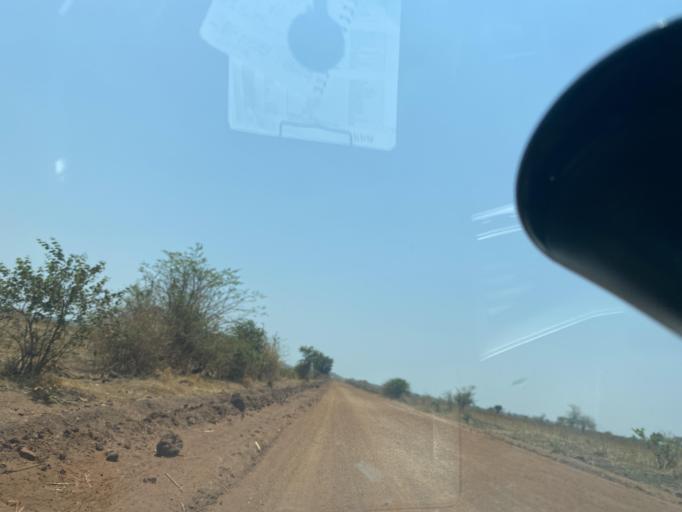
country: ZM
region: Lusaka
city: Lusaka
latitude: -15.4638
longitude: 27.9105
